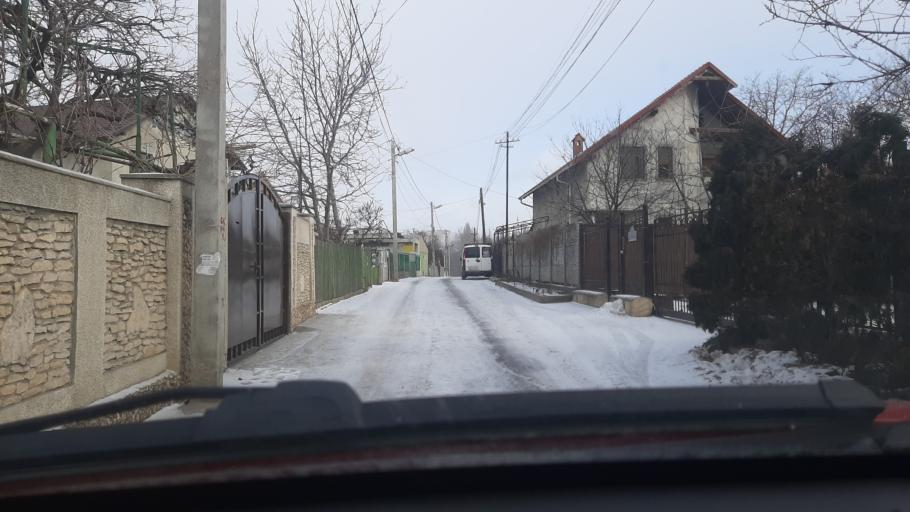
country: MD
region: Laloveni
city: Ialoveni
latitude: 46.9932
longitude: 28.7782
